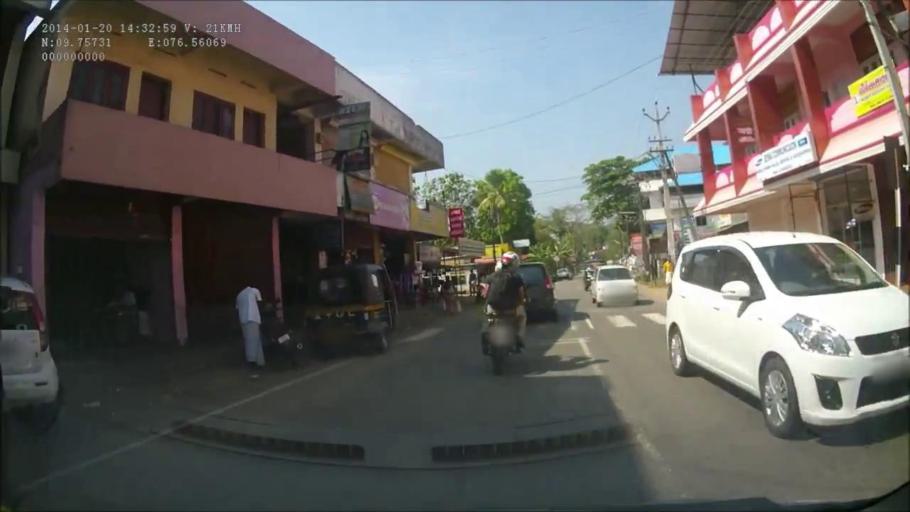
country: IN
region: Kerala
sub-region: Kottayam
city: Palackattumala
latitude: 9.7568
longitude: 76.5599
